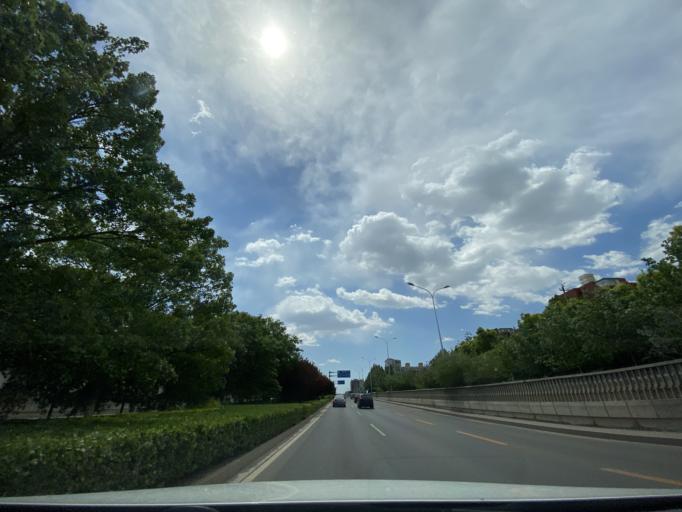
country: CN
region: Beijing
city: Sijiqing
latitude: 39.9312
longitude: 116.2468
